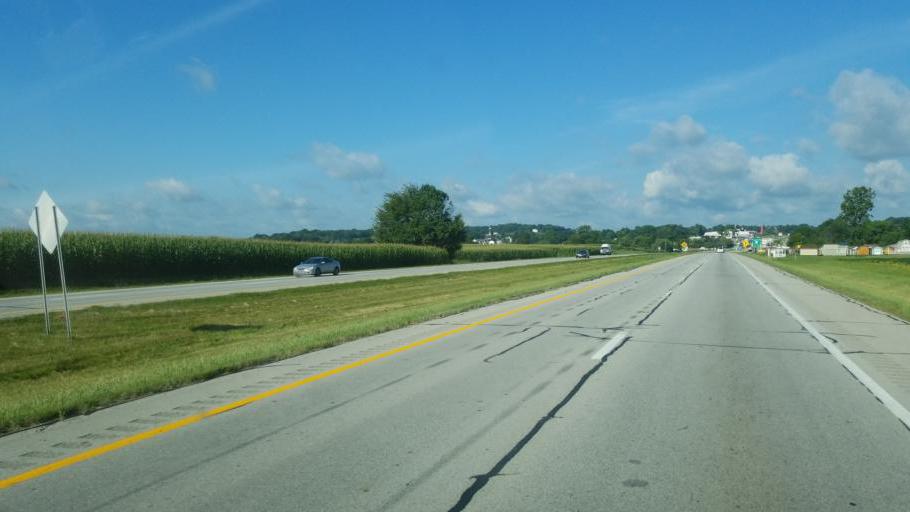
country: US
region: Ohio
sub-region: Wayne County
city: Dalton
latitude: 40.7962
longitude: -81.6816
